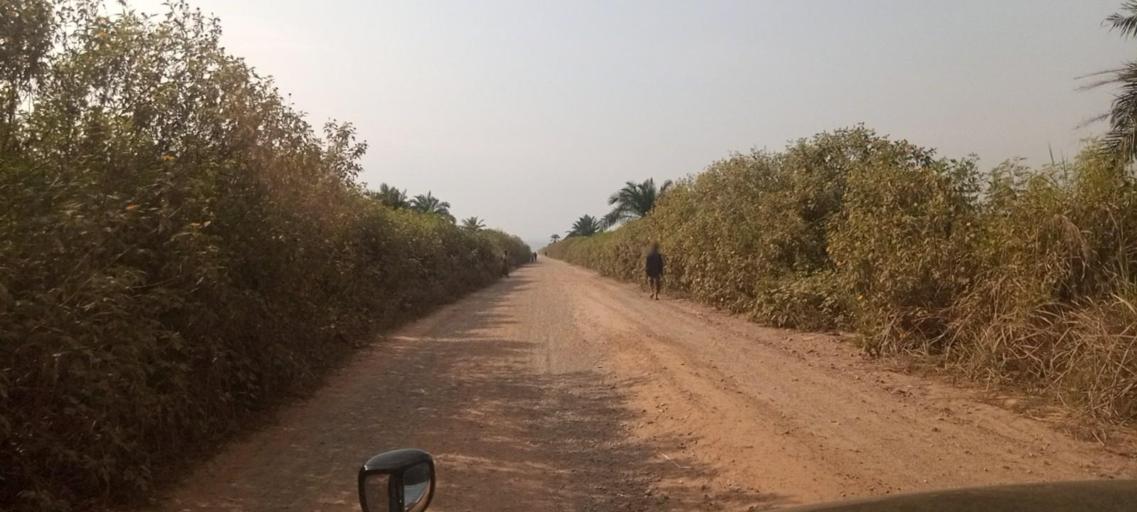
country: CD
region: Kasai-Oriental
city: Mbuji-Mayi
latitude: -6.3629
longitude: 23.8178
